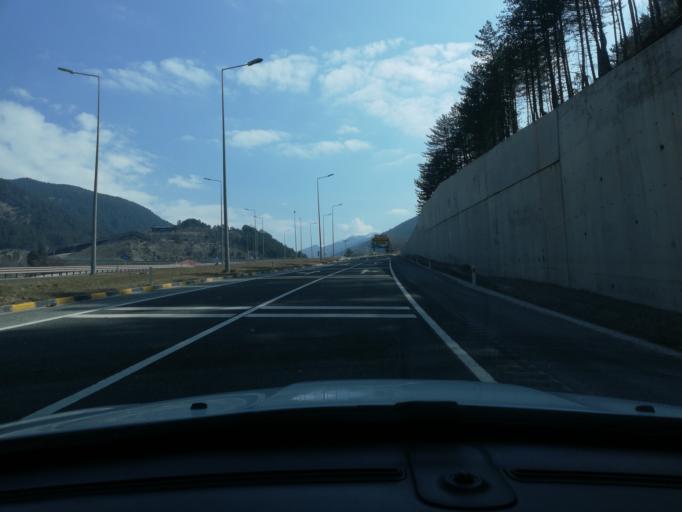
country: TR
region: Cankiri
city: Ilgaz
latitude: 41.0316
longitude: 33.7407
